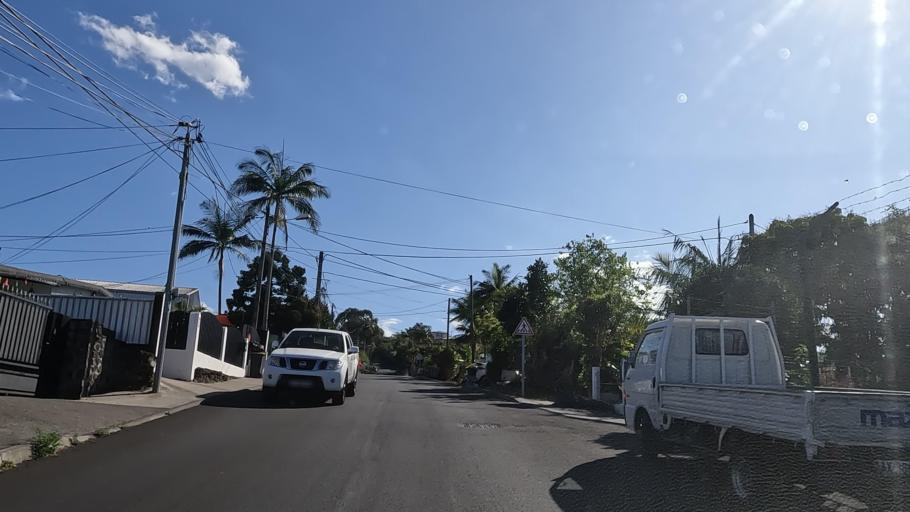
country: RE
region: Reunion
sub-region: Reunion
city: Le Tampon
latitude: -21.2585
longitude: 55.5133
